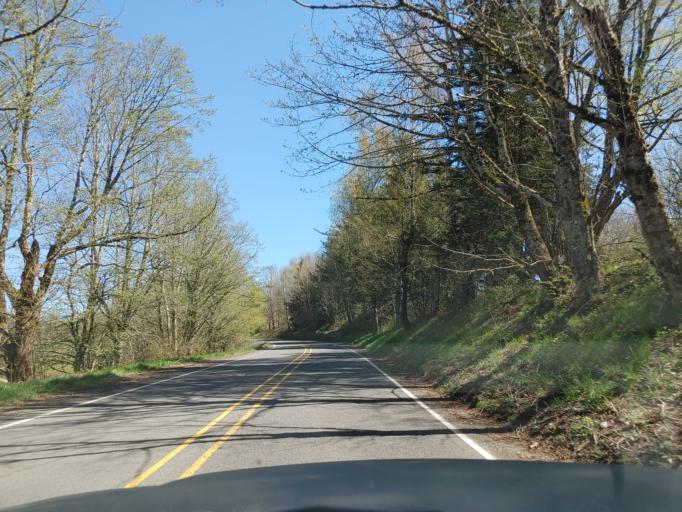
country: US
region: Washington
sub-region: Clark County
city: Washougal
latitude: 45.5299
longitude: -122.2785
